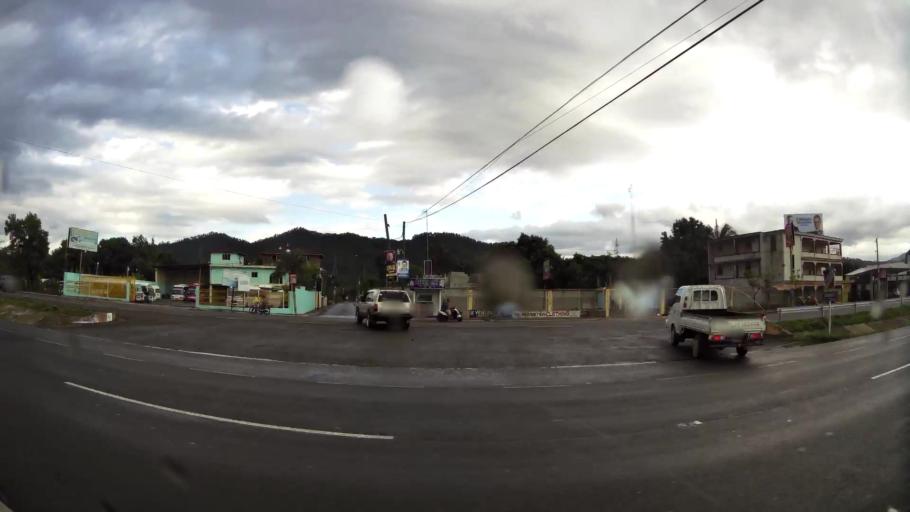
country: DO
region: Monsenor Nouel
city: Bonao
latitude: 18.9351
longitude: -70.3899
